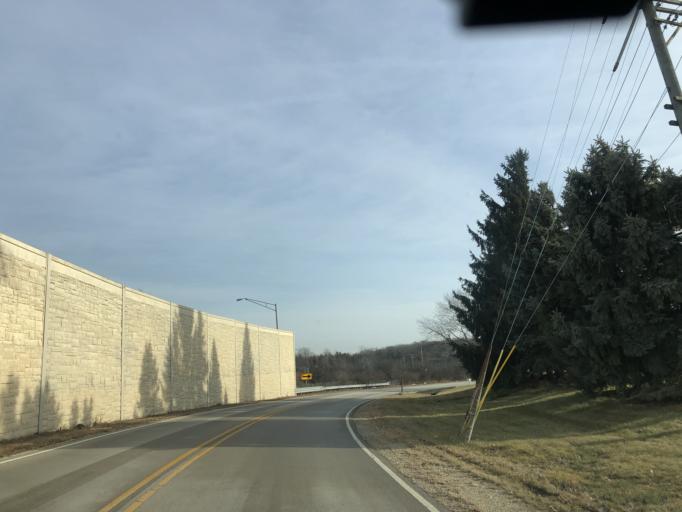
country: US
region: Illinois
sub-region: Cook County
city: Lemont
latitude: 41.7148
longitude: -88.0083
